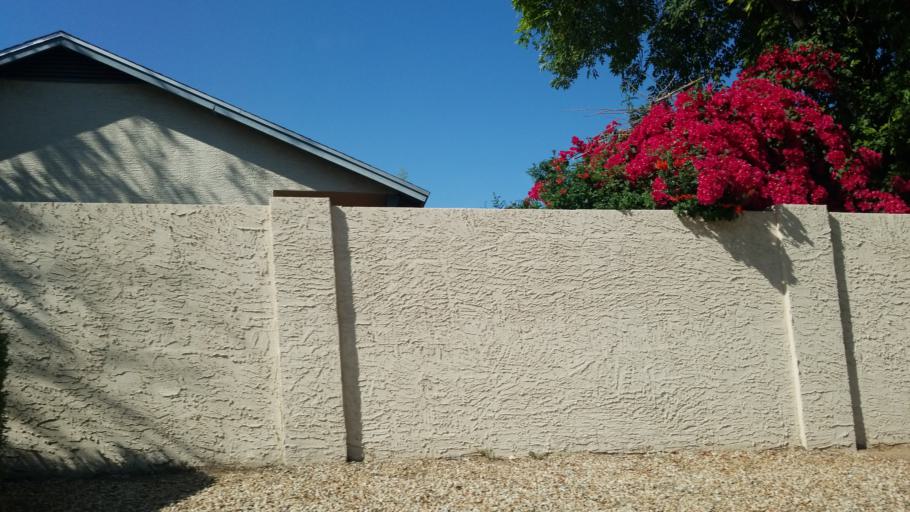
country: US
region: Arizona
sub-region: Maricopa County
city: Glendale
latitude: 33.5637
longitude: -112.1975
